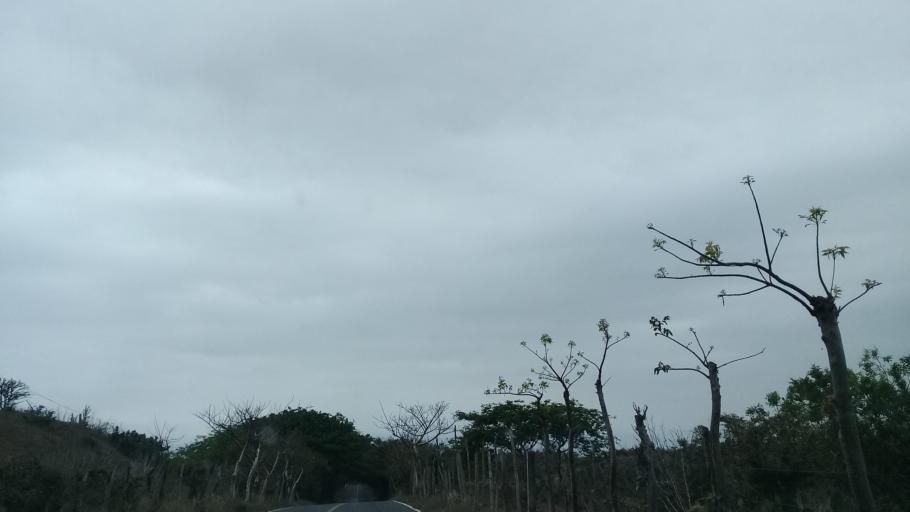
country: MX
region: Veracruz
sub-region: La Antigua
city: Nicolas Blanco (San Pancho)
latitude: 19.3361
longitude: -96.3266
